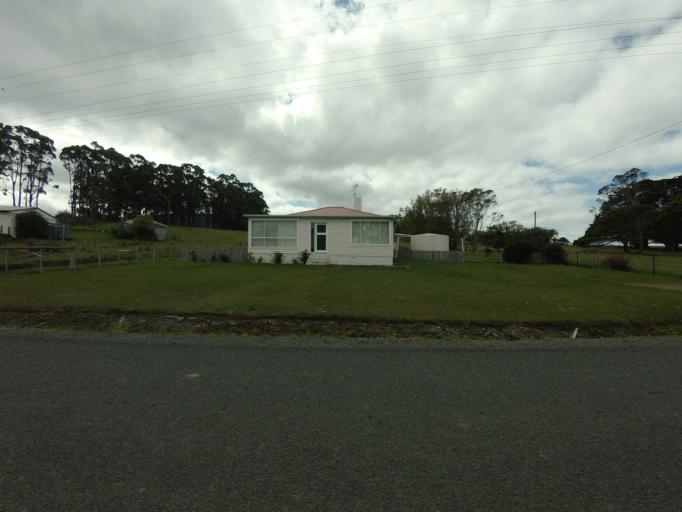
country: AU
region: Tasmania
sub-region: Huon Valley
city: Geeveston
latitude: -43.4324
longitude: 146.9772
